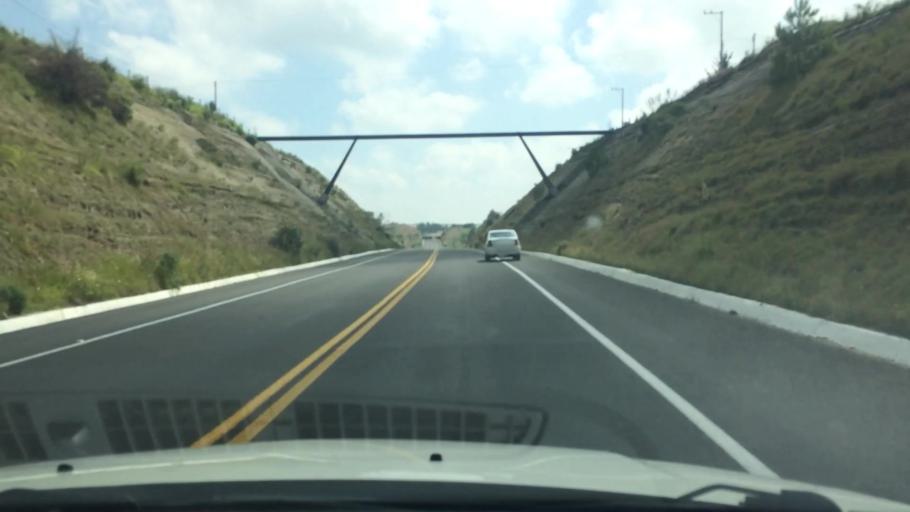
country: MX
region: Mexico
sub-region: Villa Victoria
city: Colonia Doctor Gustavo Baz
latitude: 19.3762
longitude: -99.8905
